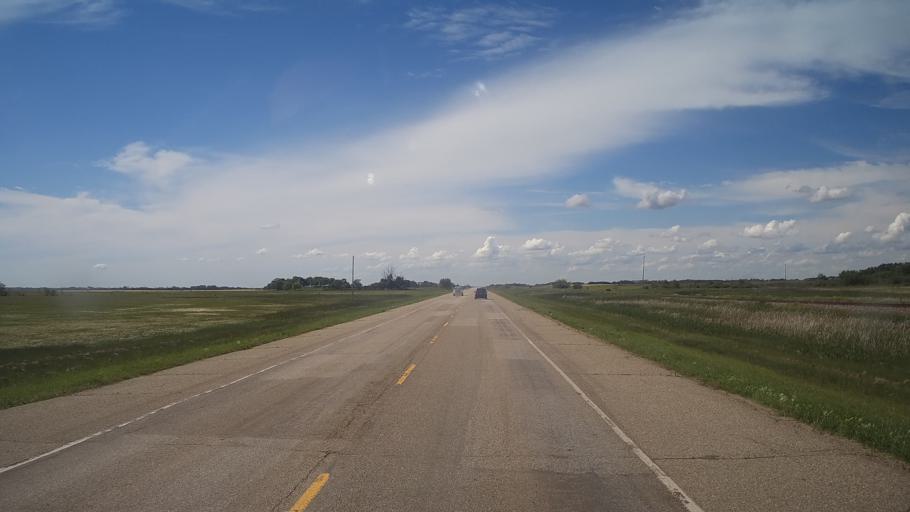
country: CA
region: Saskatchewan
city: Yorkton
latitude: 51.0648
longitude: -102.2133
